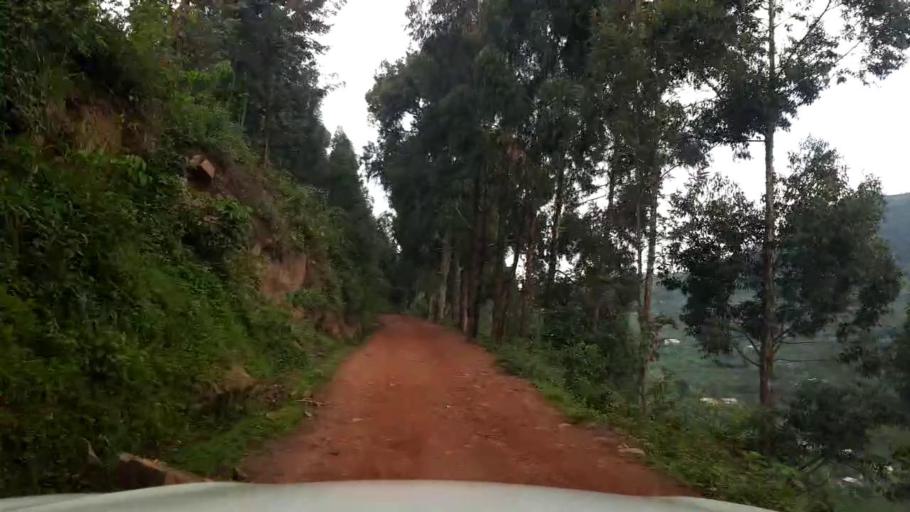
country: UG
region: Western Region
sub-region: Kisoro District
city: Kisoro
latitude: -1.3993
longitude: 29.8014
